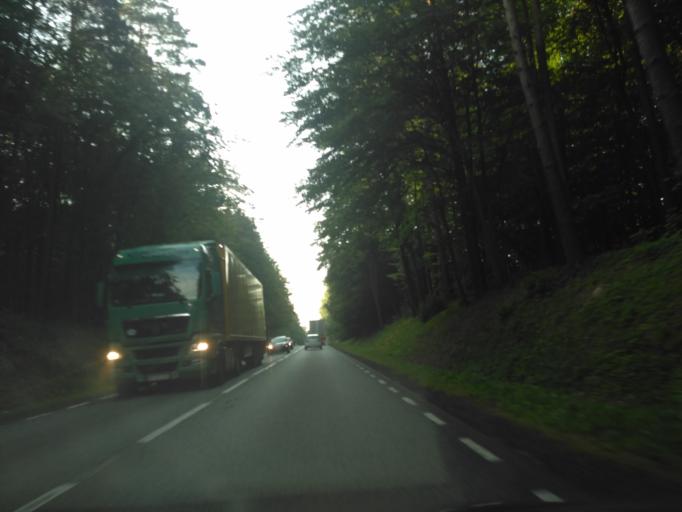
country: PL
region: Lublin Voivodeship
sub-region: Powiat krasnicki
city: Szastarka
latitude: 50.8510
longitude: 22.2886
